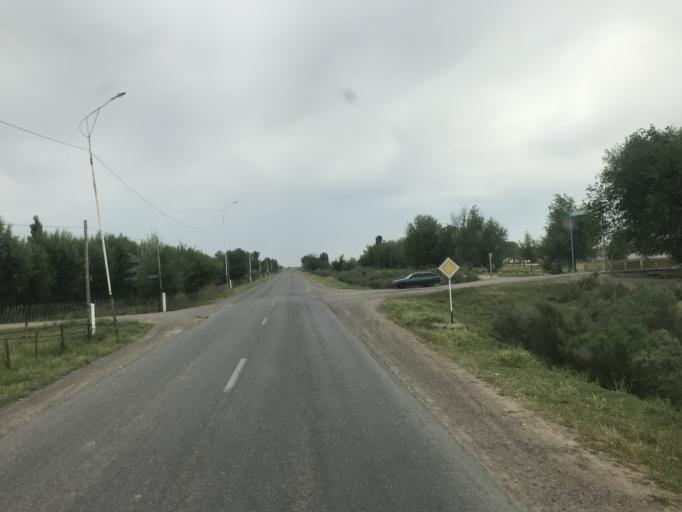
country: KZ
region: Ongtustik Qazaqstan
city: Asykata
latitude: 40.9285
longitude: 68.4054
